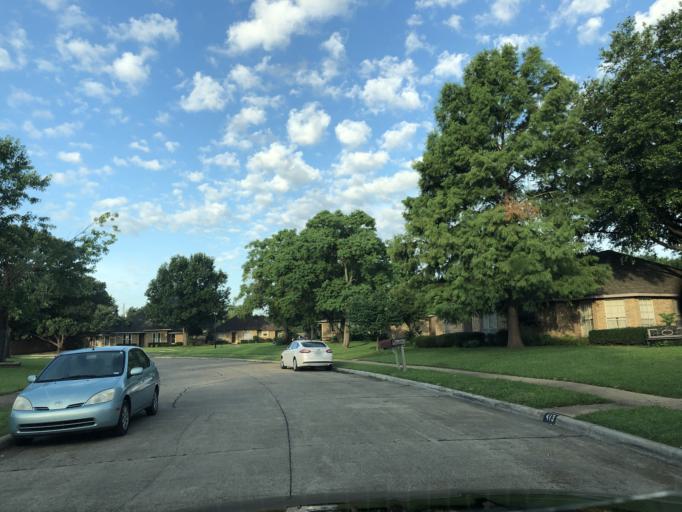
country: US
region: Texas
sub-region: Dallas County
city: Garland
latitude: 32.8502
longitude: -96.6191
